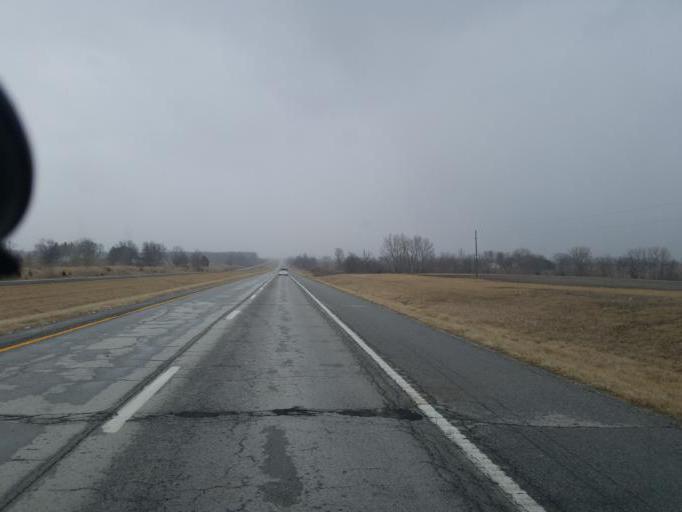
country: US
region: Missouri
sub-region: Macon County
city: La Plata
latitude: 40.0037
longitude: -92.4755
